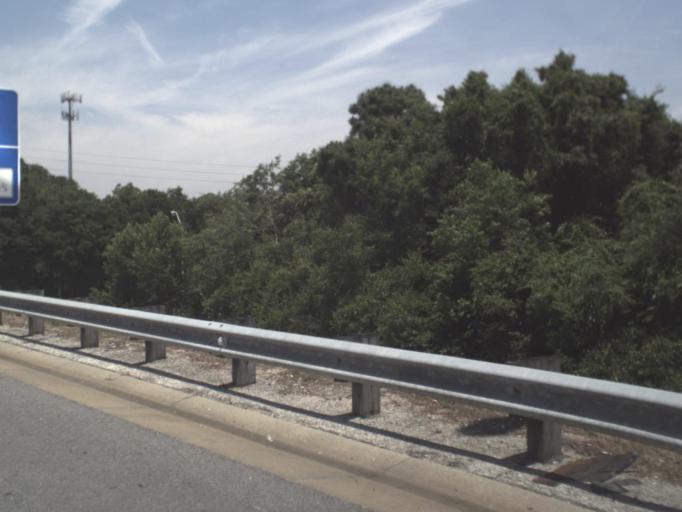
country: US
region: Florida
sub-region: Duval County
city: Jacksonville
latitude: 30.3403
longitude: -81.5409
